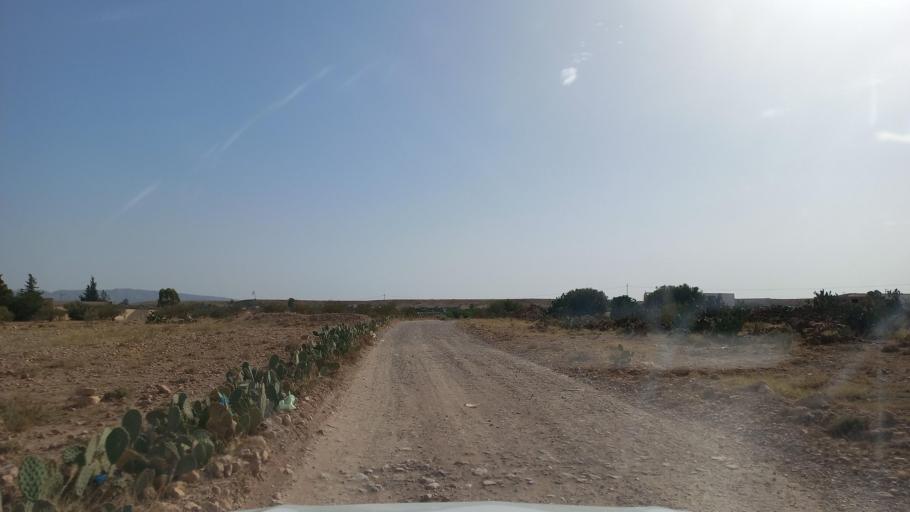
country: TN
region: Al Qasrayn
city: Kasserine
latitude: 35.2674
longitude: 8.9344
